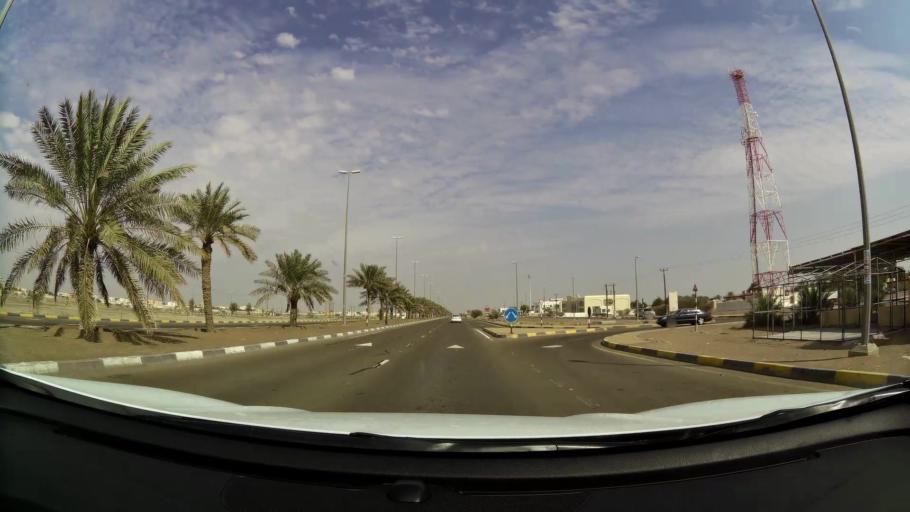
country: AE
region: Abu Dhabi
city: Al Ain
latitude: 24.0862
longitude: 55.8351
